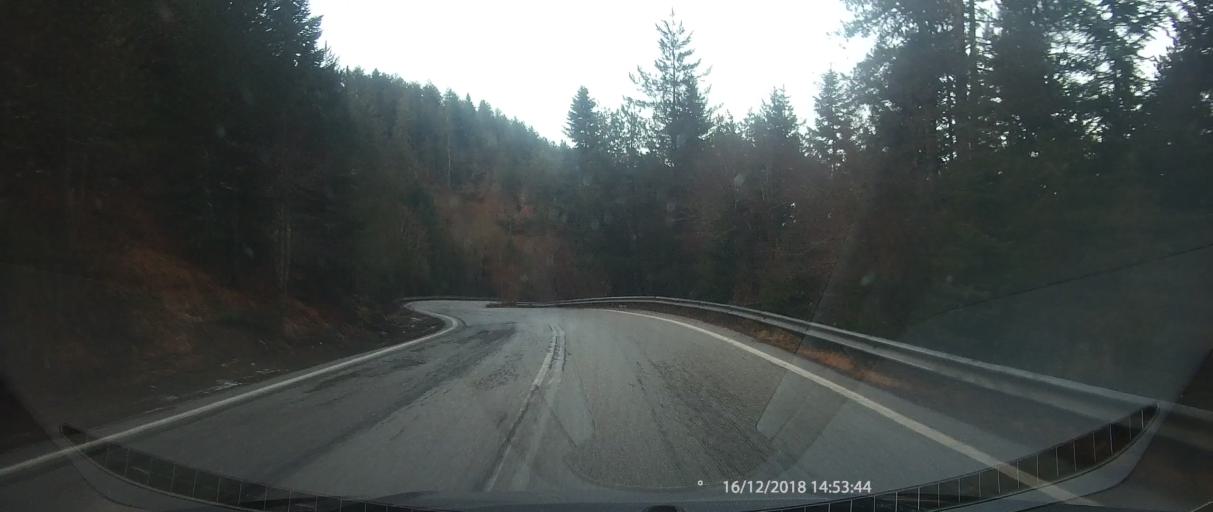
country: GR
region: West Macedonia
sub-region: Nomos Kastorias
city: Nestorio
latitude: 40.2111
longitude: 21.0556
